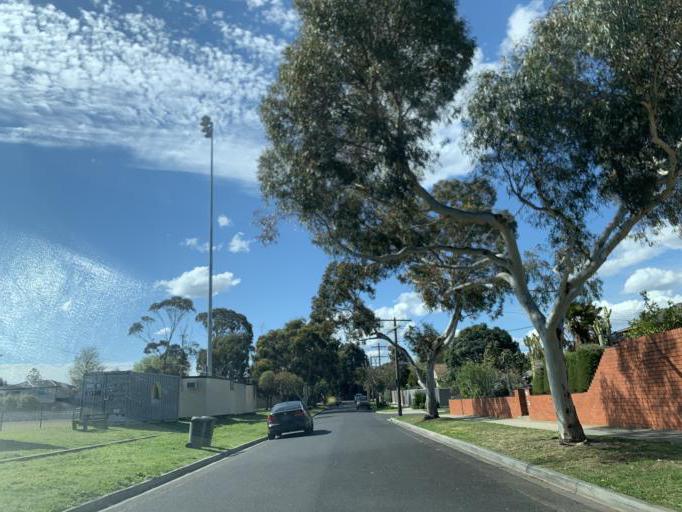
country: AU
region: Victoria
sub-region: Bayside
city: Hampton East
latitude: -37.9473
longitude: 145.0189
